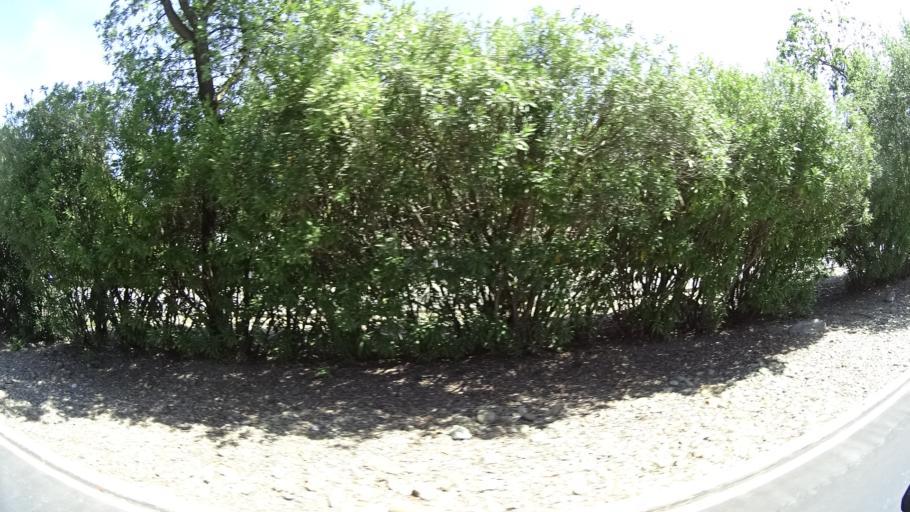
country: US
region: California
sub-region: Placer County
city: Rocklin
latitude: 38.7967
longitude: -121.2510
